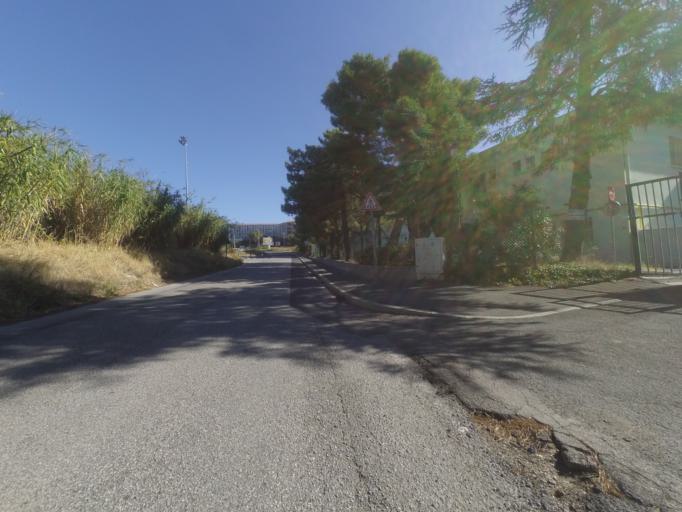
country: FR
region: Languedoc-Roussillon
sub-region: Departement des Pyrenees-Orientales
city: Perpignan
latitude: 42.6799
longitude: 2.8950
